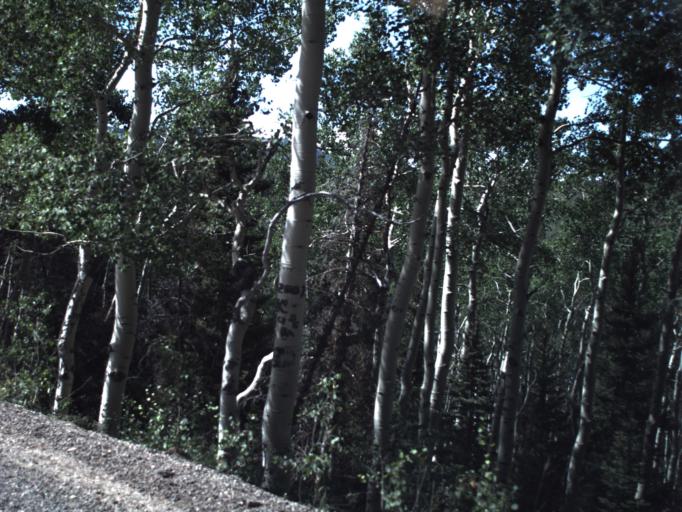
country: US
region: Utah
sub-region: Piute County
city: Junction
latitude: 38.2579
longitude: -112.3790
